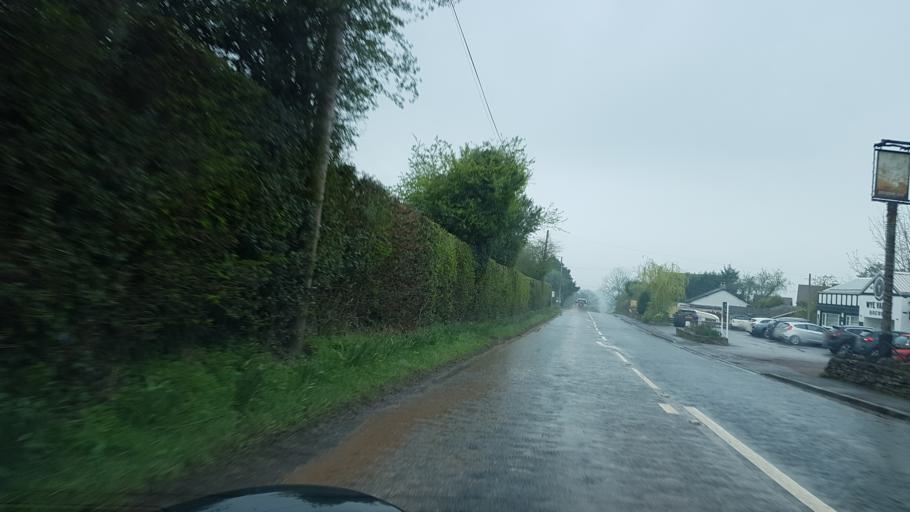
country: GB
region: England
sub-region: Herefordshire
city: Moreton Jeffries
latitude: 52.1493
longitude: -2.5509
